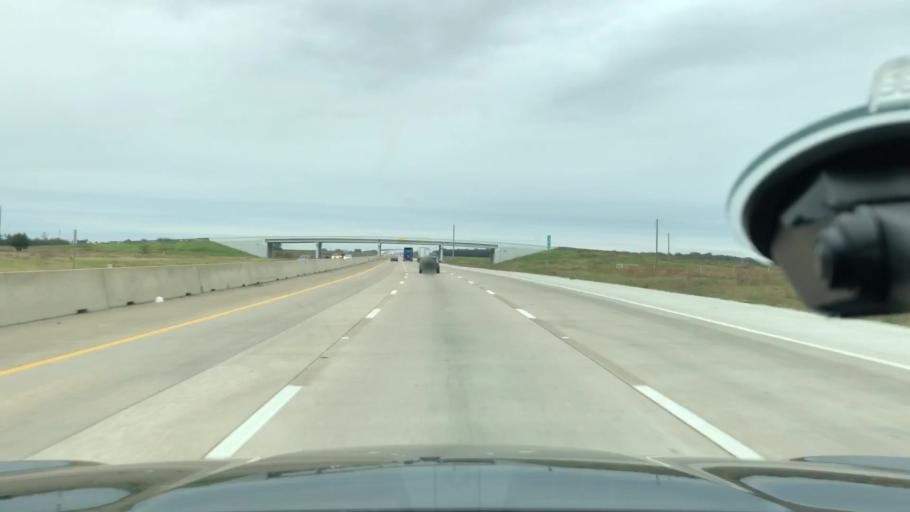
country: US
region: Texas
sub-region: Ellis County
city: Italy
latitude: 32.2439
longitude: -96.8760
